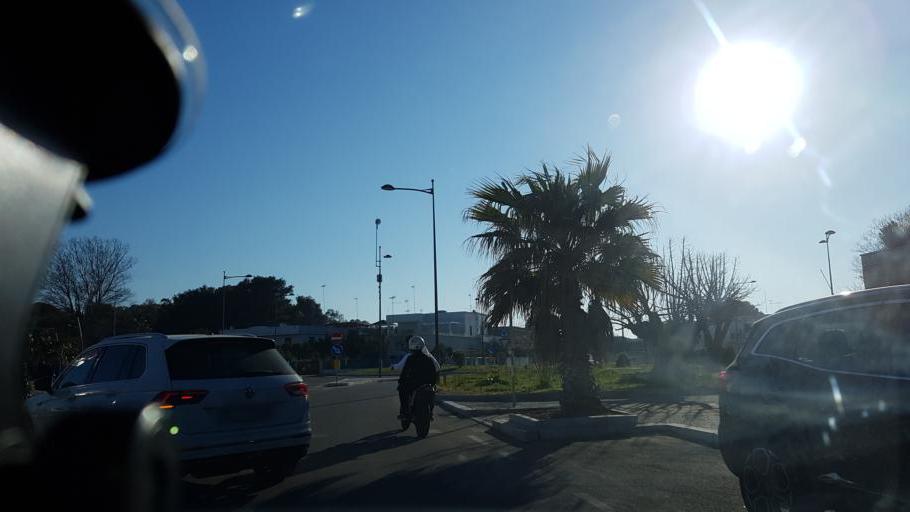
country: IT
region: Apulia
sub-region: Provincia di Lecce
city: Struda
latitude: 40.3881
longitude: 18.3045
